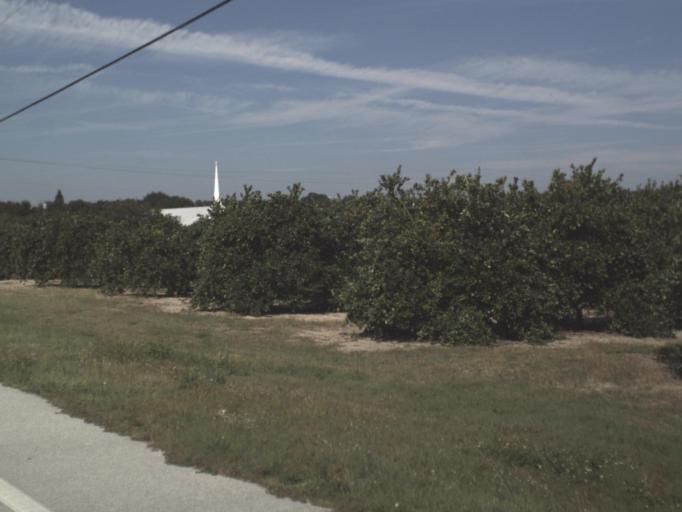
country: US
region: Florida
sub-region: Highlands County
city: Avon Park
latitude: 27.5883
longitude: -81.4806
